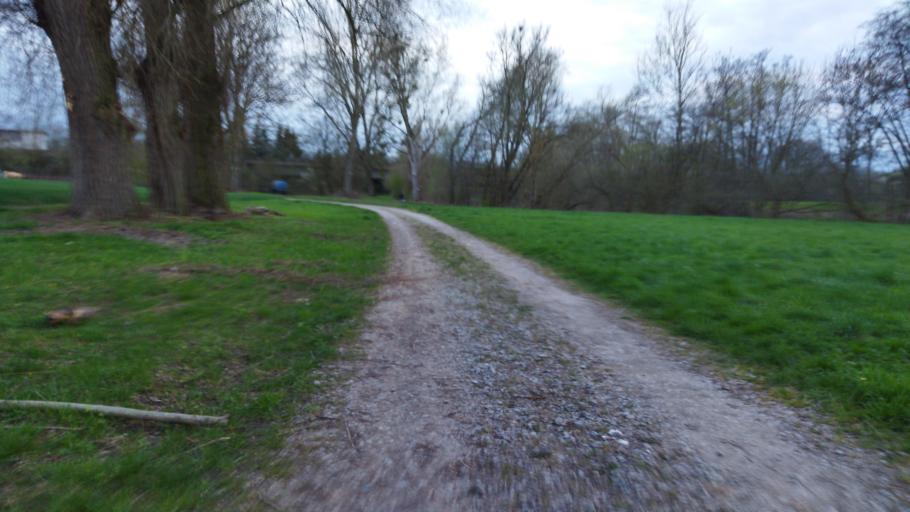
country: DE
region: Baden-Wuerttemberg
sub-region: Regierungsbezirk Stuttgart
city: Offenau
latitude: 49.2387
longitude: 9.1883
